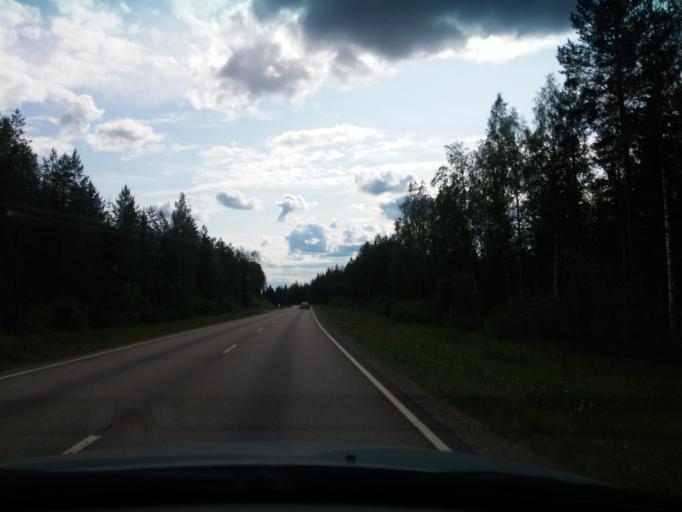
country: FI
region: Central Finland
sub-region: Keuruu
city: Multia
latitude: 62.3802
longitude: 24.7489
